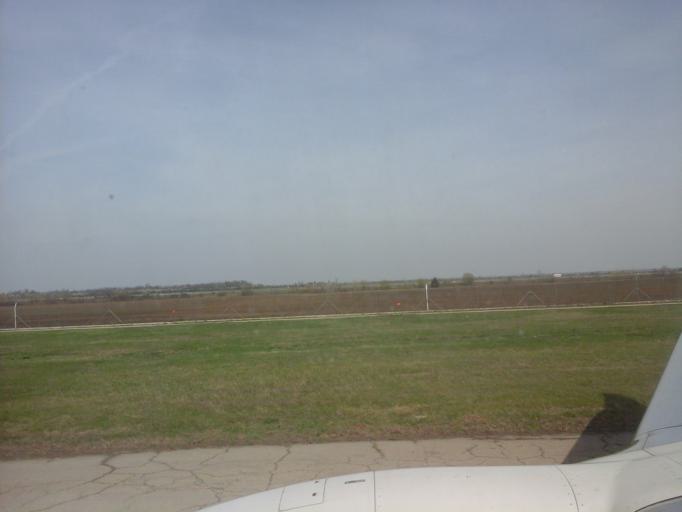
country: RO
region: Ilfov
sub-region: Comuna Otopeni
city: Otopeni
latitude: 44.5706
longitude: 26.1042
